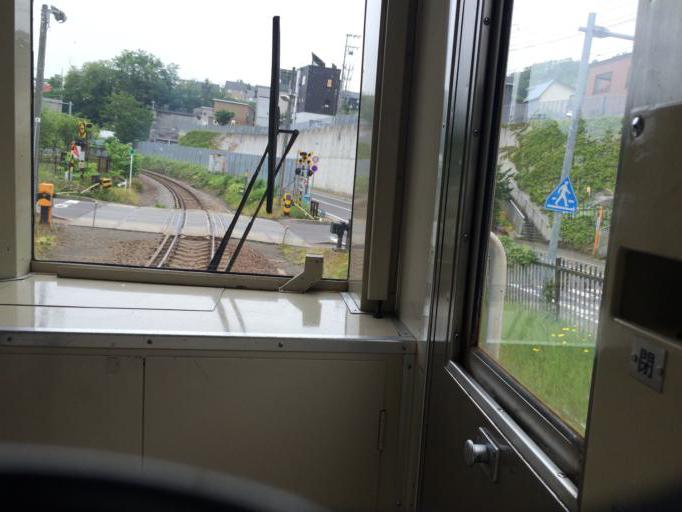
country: JP
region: Hokkaido
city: Otaru
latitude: 43.2023
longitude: 140.9854
